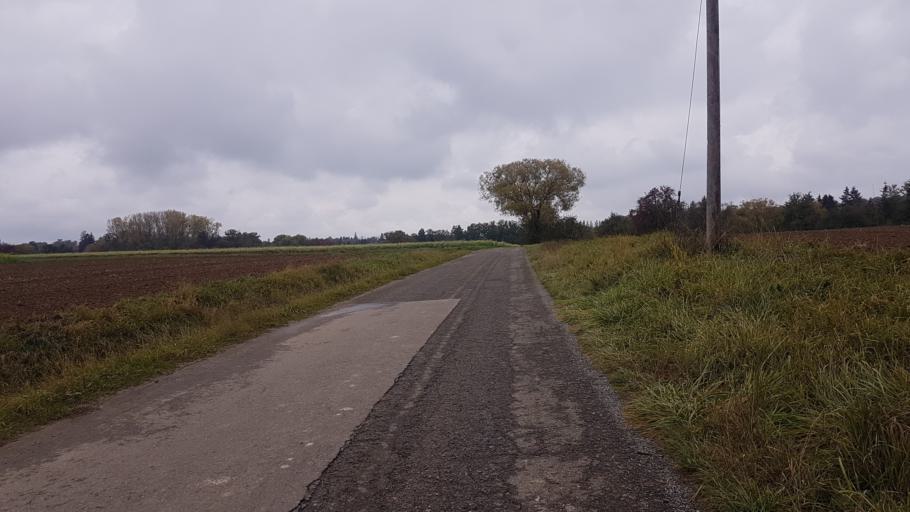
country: DE
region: Baden-Wuerttemberg
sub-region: Tuebingen Region
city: Dusslingen
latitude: 48.4610
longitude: 9.0455
